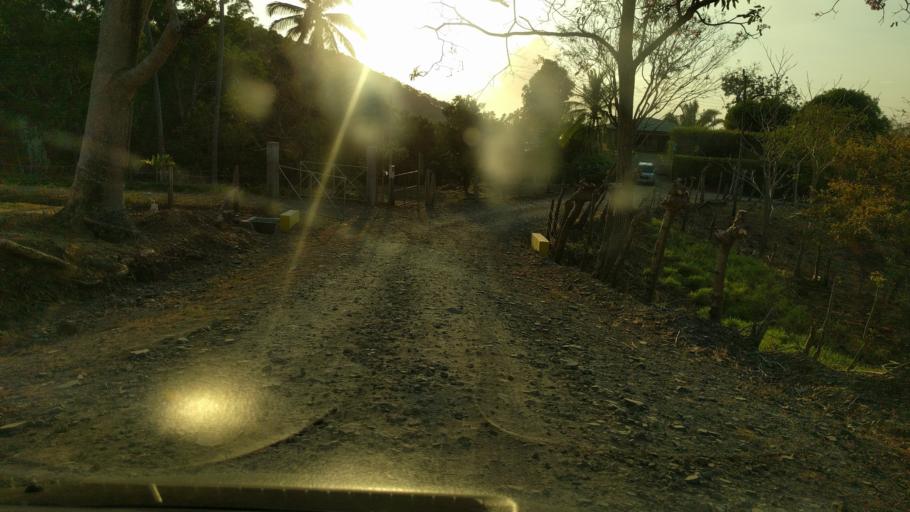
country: CR
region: Puntarenas
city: Esparza
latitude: 10.0327
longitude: -84.6977
